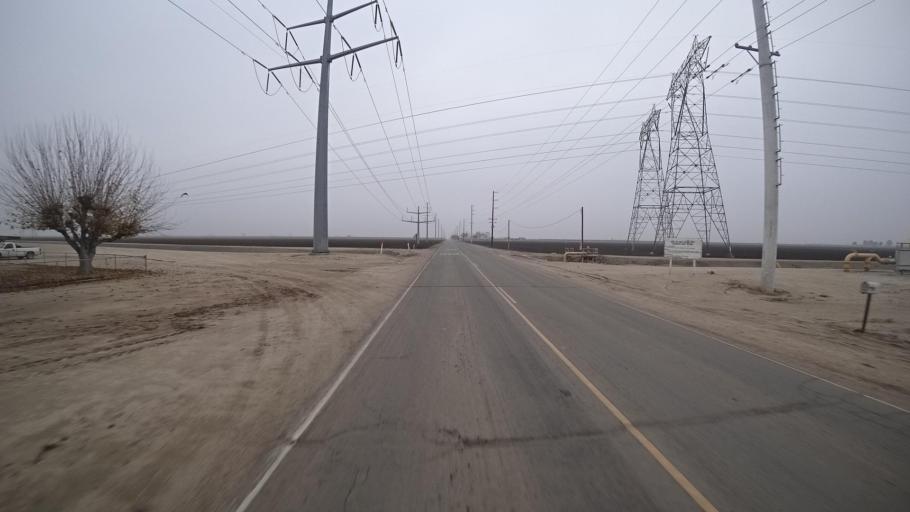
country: US
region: California
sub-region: Kern County
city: Buttonwillow
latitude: 35.3972
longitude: -119.4476
